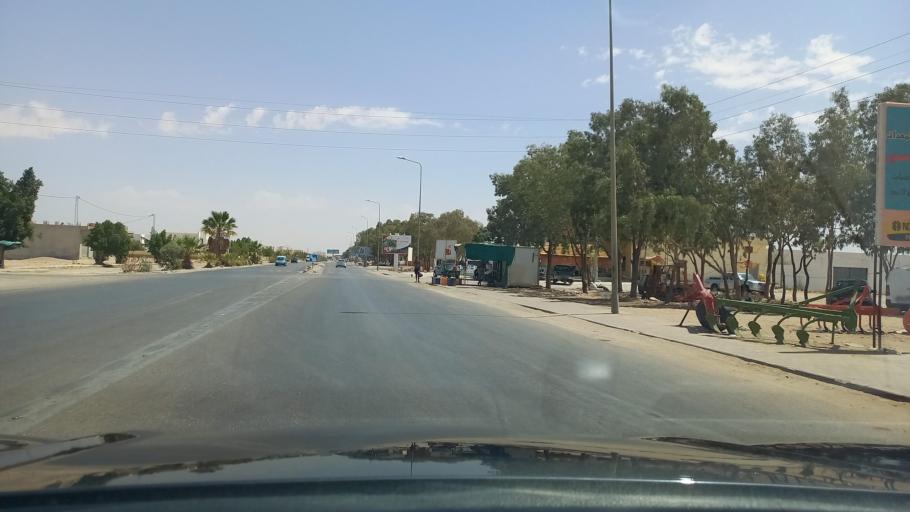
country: TN
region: Madanin
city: Medenine
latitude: 33.3633
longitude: 10.4630
